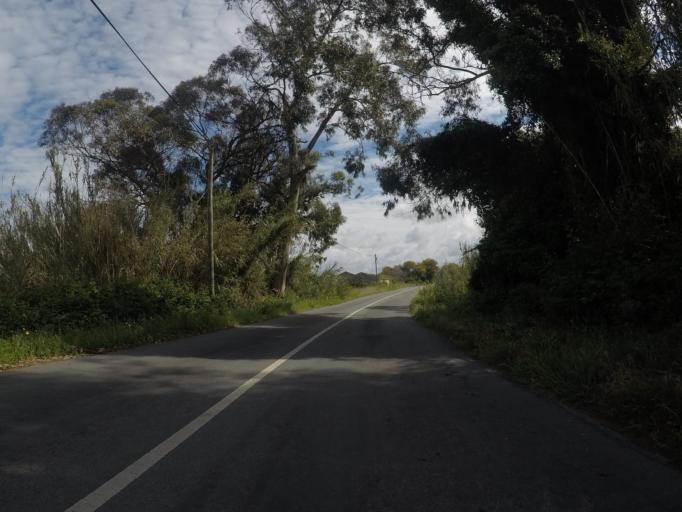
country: PT
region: Beja
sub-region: Odemira
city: Sao Teotonio
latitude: 37.4773
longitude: -8.7862
